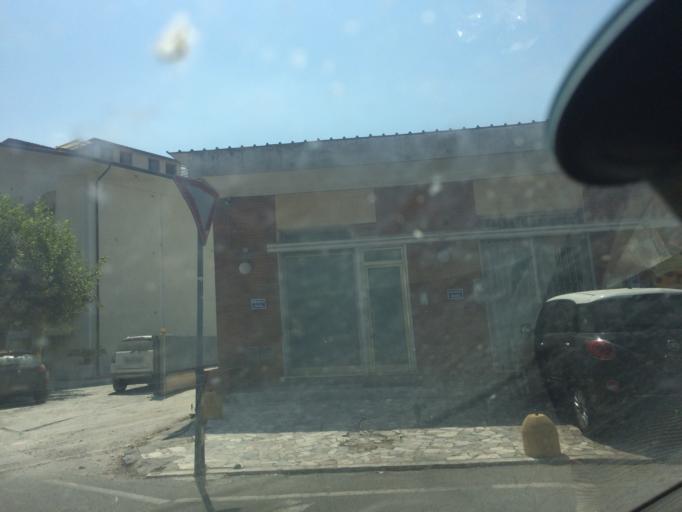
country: IT
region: Tuscany
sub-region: Provincia di Massa-Carrara
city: Massa
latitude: 44.0213
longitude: 10.0896
